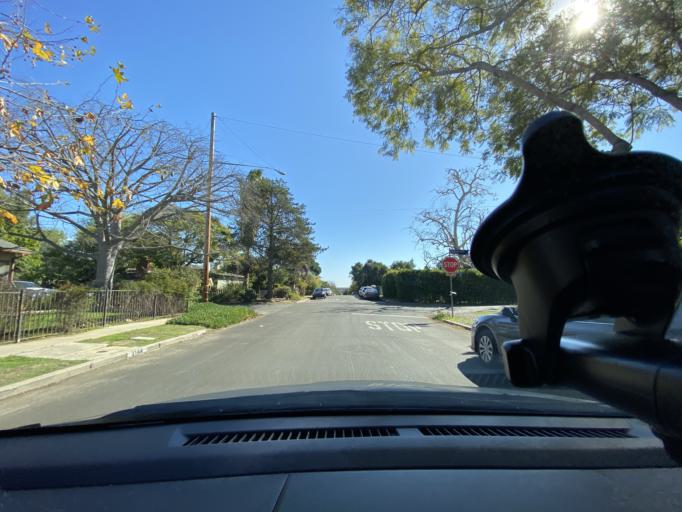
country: US
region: California
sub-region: Los Angeles County
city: Culver City
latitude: 34.0274
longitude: -118.4210
